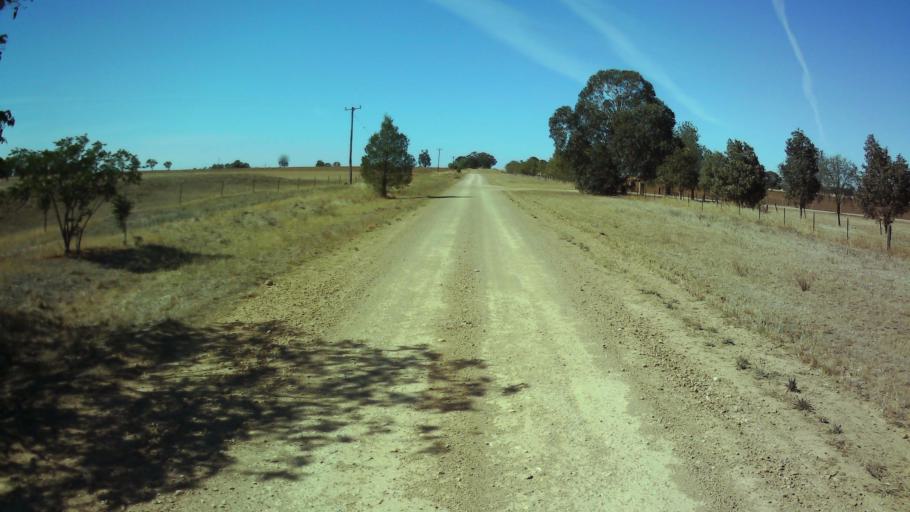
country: AU
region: New South Wales
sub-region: Weddin
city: Grenfell
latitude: -34.0574
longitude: 148.1716
